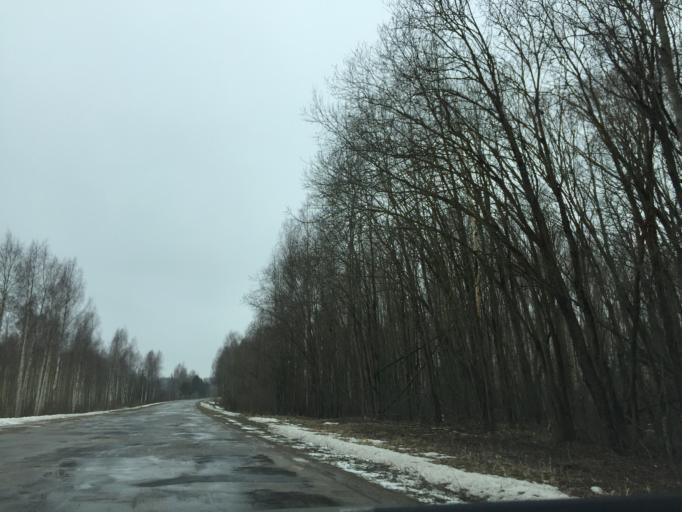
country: LV
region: Lecava
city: Iecava
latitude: 56.5803
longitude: 24.0801
